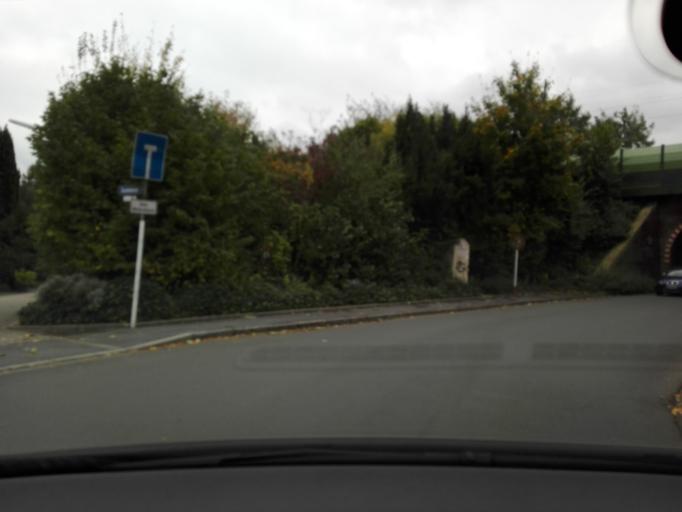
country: DE
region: North Rhine-Westphalia
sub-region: Regierungsbezirk Arnsberg
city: Holzwickede
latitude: 51.4958
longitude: 7.5956
